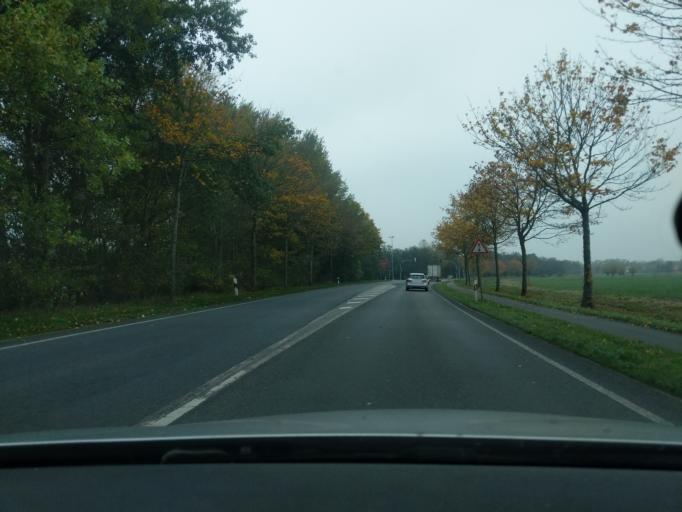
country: DE
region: Lower Saxony
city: Cuxhaven
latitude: 53.8326
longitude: 8.7407
